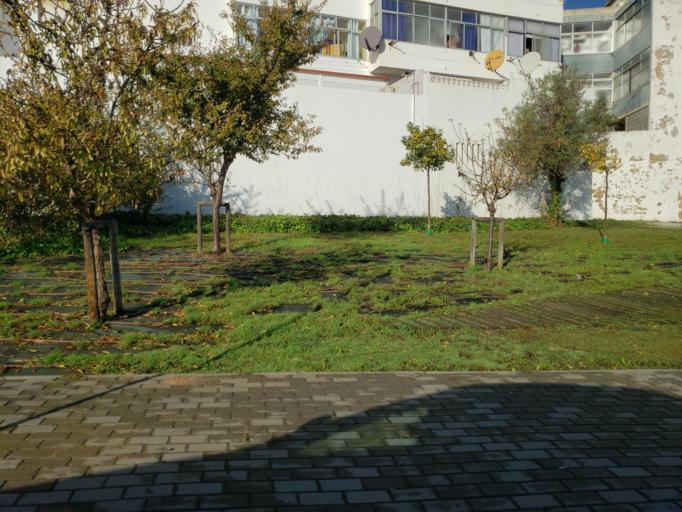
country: PT
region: Faro
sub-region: Portimao
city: Portimao
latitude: 37.1491
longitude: -8.5508
